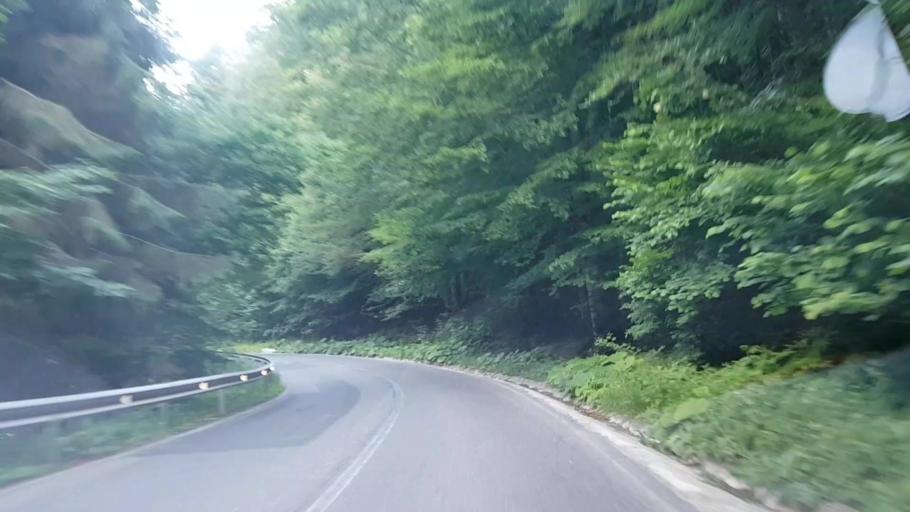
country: RO
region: Harghita
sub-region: Comuna Praid
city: Ocna de Sus
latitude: 46.6002
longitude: 25.2390
